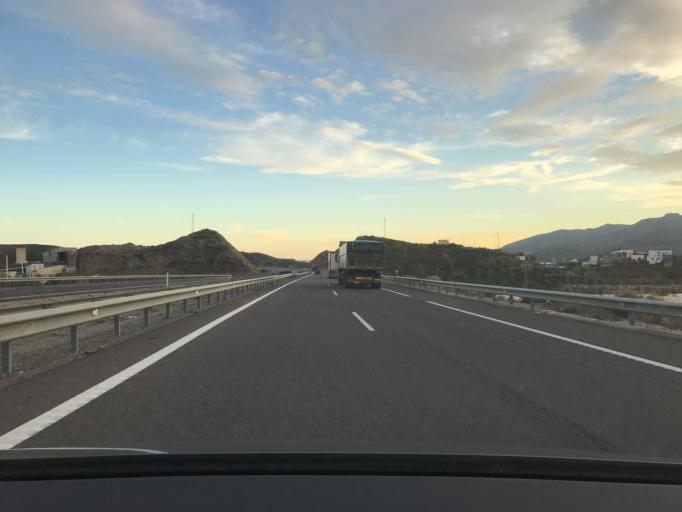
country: ES
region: Andalusia
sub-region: Provincia de Almeria
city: Rioja
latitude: 36.9395
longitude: -2.4485
